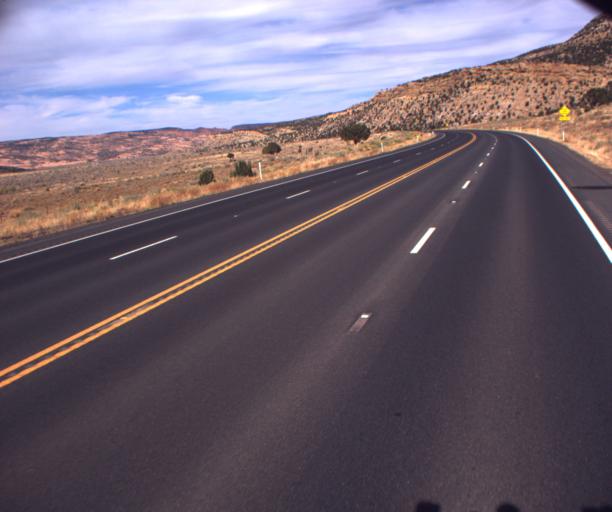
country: US
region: Arizona
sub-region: Navajo County
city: Kayenta
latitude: 36.5769
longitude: -110.4746
